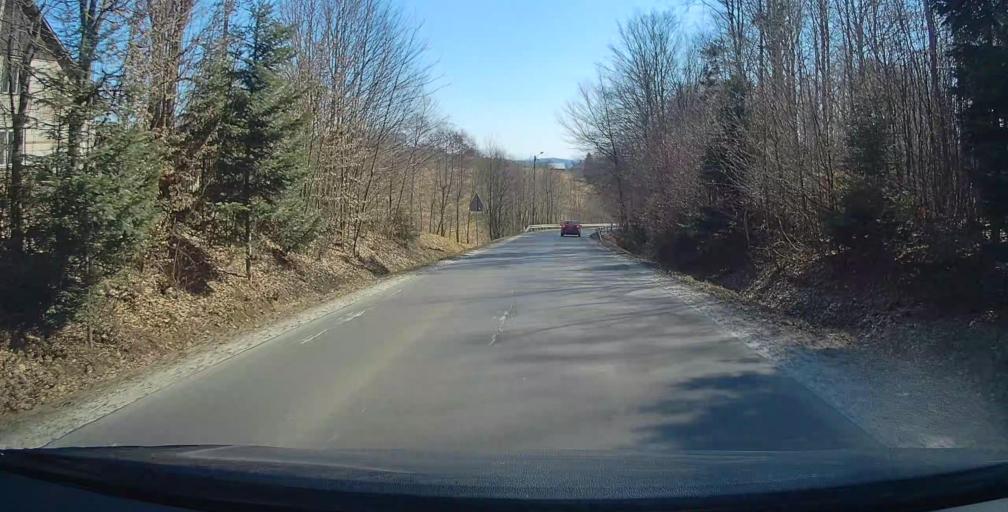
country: PL
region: Subcarpathian Voivodeship
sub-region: Powiat rzeszowski
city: Hyzne
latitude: 49.8949
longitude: 22.2225
